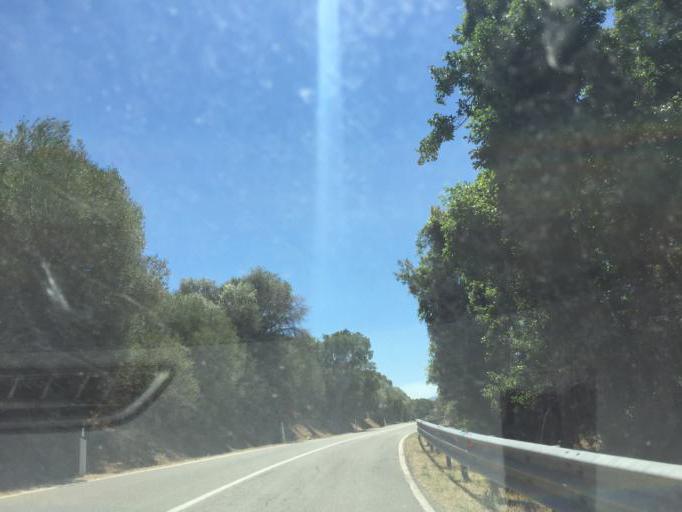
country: IT
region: Sardinia
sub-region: Provincia di Olbia-Tempio
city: Telti
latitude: 40.8974
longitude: 9.2936
